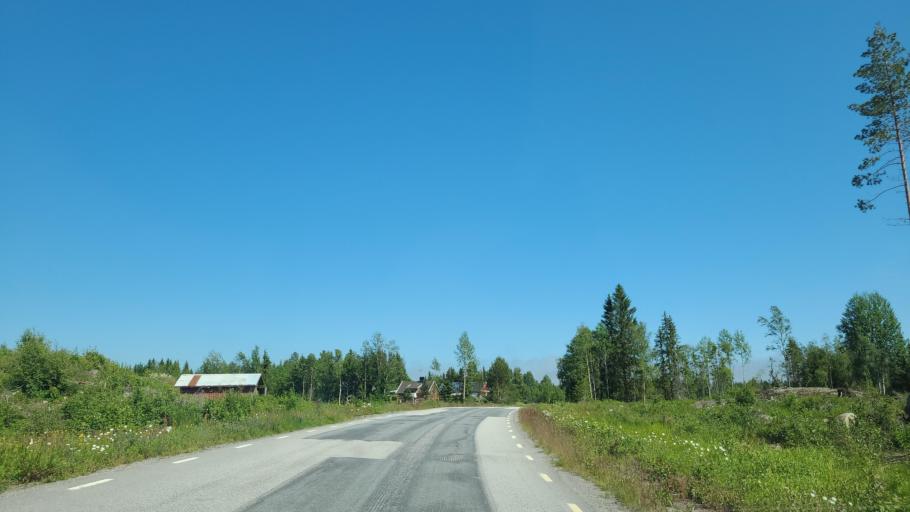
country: SE
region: Vaesternorrland
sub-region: OErnskoeldsviks Kommun
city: Husum
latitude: 63.3891
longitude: 19.2080
